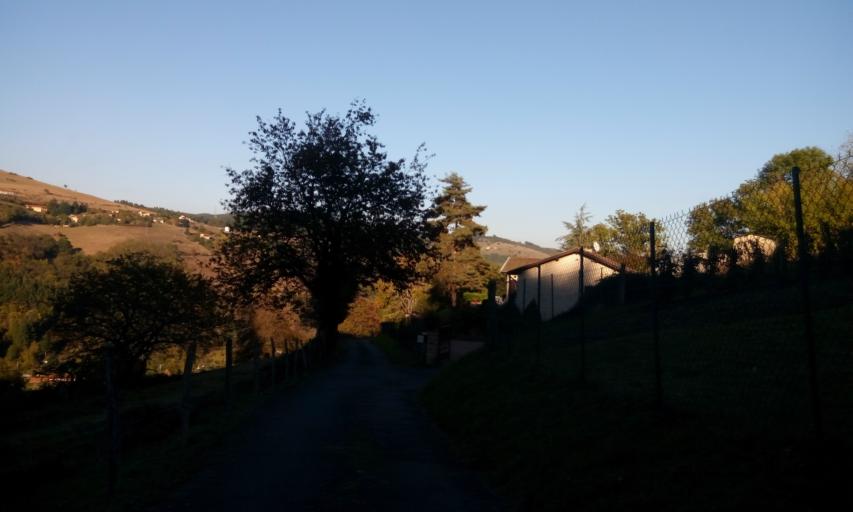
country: FR
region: Rhone-Alpes
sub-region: Departement du Rhone
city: Tarare
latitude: 45.9174
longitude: 4.4621
